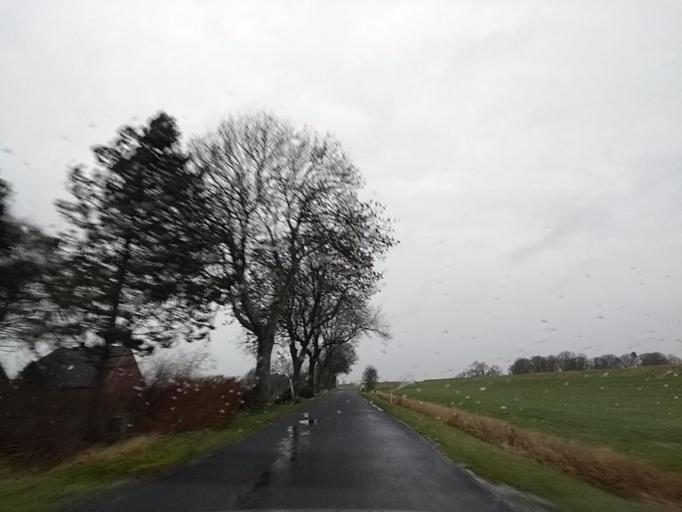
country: DE
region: Lower Saxony
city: Bunde
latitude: 53.2492
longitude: 7.2395
